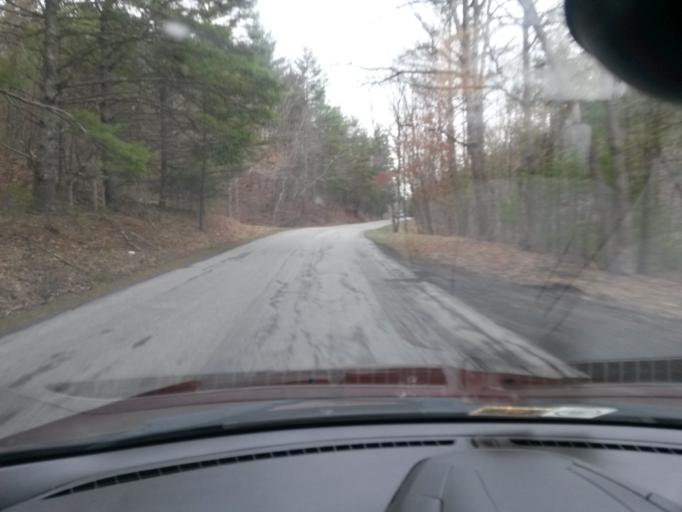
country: US
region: Virginia
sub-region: Bath County
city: Warm Springs
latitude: 38.0274
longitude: -79.8600
